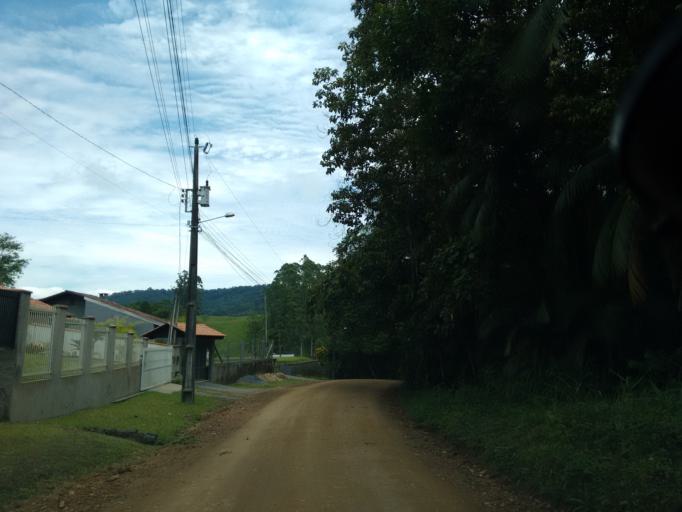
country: BR
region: Santa Catarina
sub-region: Pomerode
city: Pomerode
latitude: -26.8079
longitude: -49.1565
